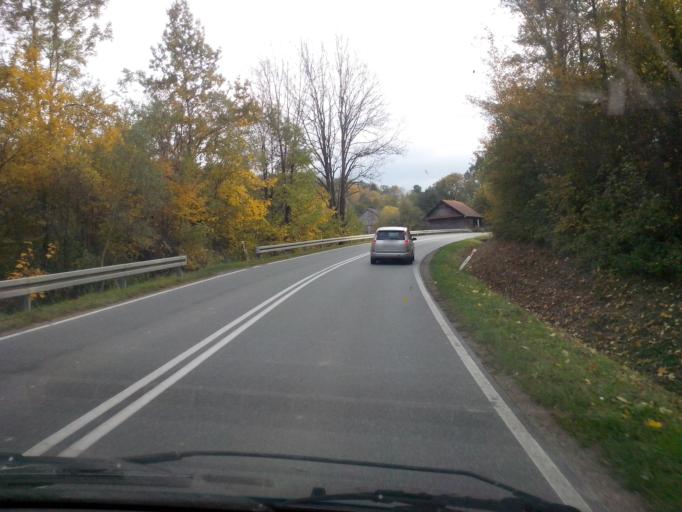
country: PL
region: Subcarpathian Voivodeship
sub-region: Powiat strzyzowski
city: Wisniowa
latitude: 49.8854
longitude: 21.6475
